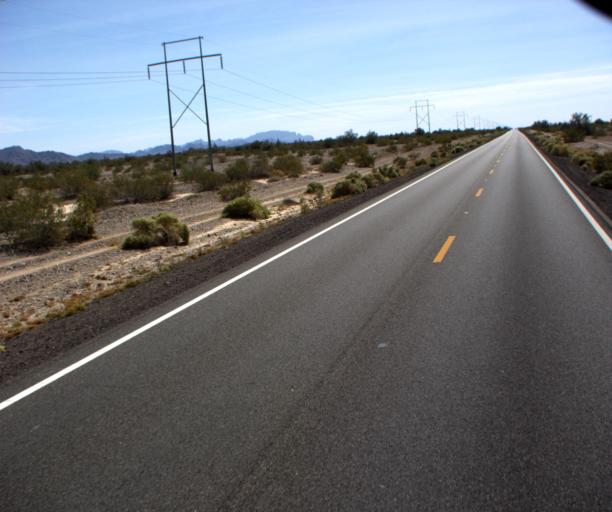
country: US
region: Arizona
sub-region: La Paz County
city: Quartzsite
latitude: 33.6406
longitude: -114.2171
